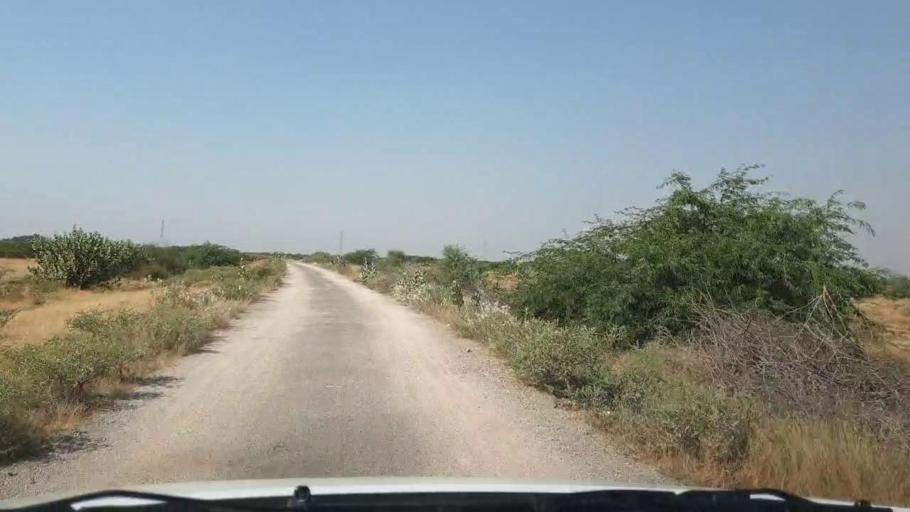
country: PK
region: Sindh
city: Gharo
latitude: 24.7966
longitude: 67.4911
